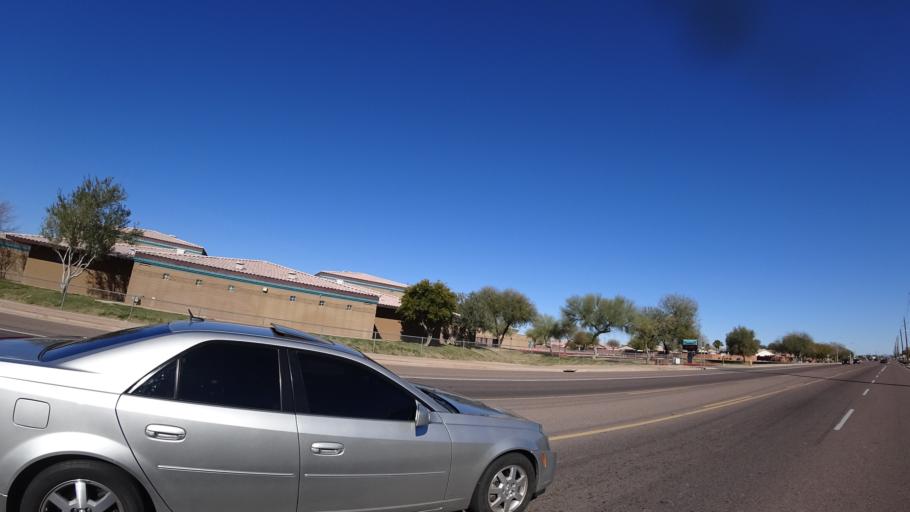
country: US
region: Arizona
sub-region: Maricopa County
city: Tolleson
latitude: 33.4229
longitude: -112.2163
